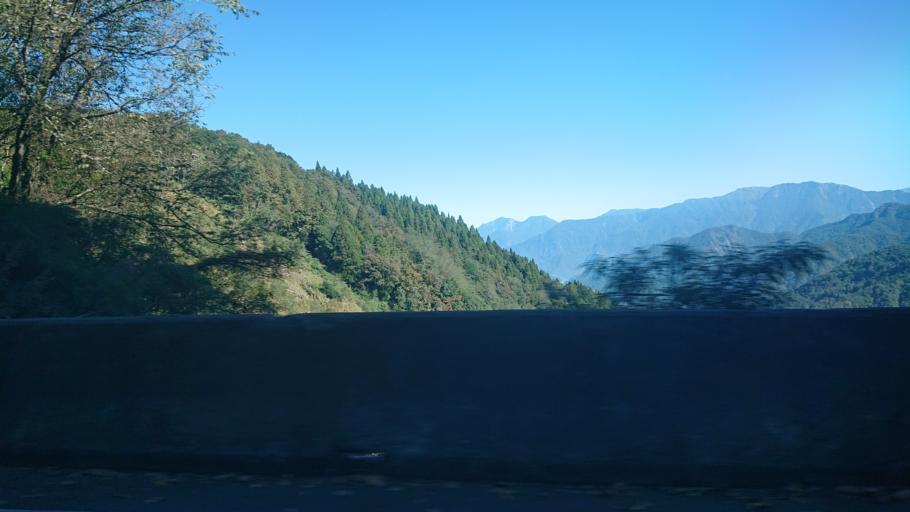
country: TW
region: Taiwan
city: Lugu
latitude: 23.4829
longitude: 120.8306
